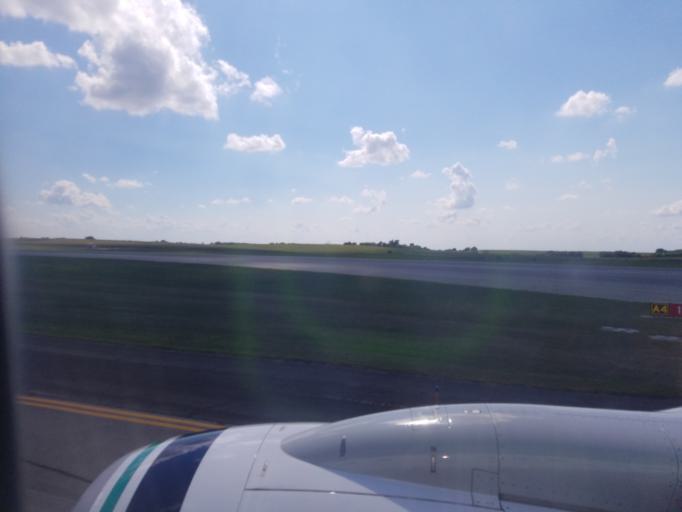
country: US
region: Missouri
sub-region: Platte County
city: Weatherby Lake
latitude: 39.3108
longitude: -94.7225
